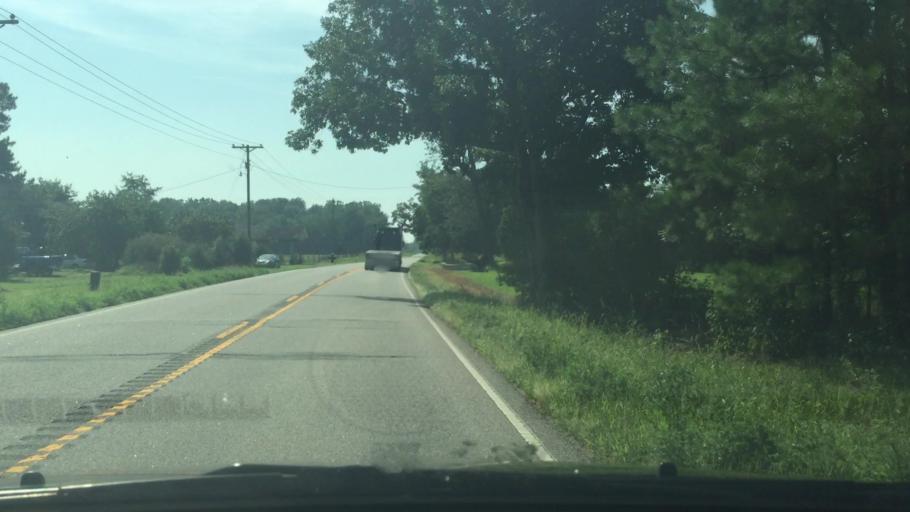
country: US
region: Virginia
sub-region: Sussex County
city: Sussex
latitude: 36.9980
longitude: -77.2621
